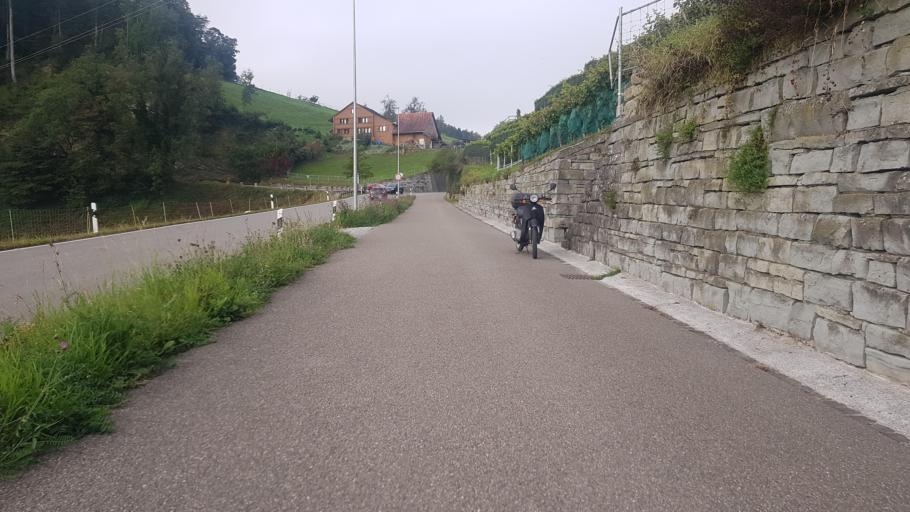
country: CH
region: Appenzell Ausserrhoden
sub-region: Bezirk Vorderland
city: Heiden
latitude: 47.4714
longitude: 9.5537
